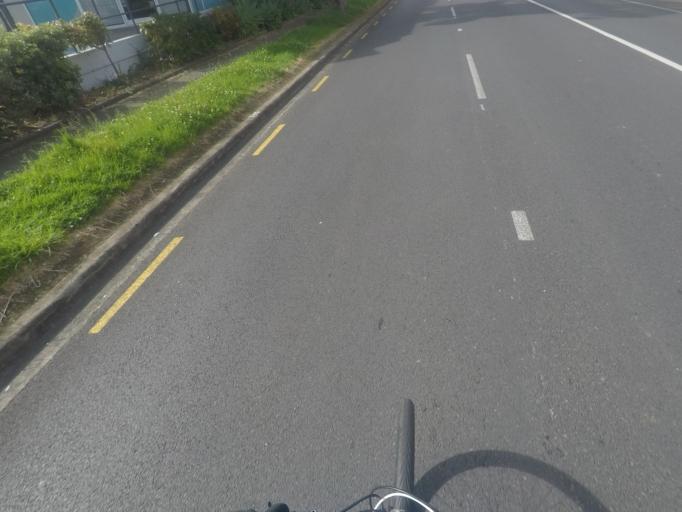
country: NZ
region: Auckland
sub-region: Auckland
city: Mangere
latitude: -36.9233
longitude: 174.7832
